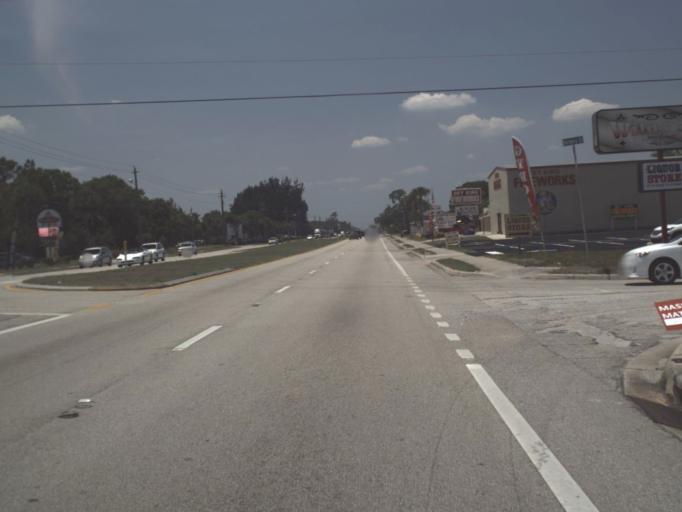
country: US
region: Florida
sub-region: Brevard County
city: June Park
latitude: 28.0790
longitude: -80.6766
